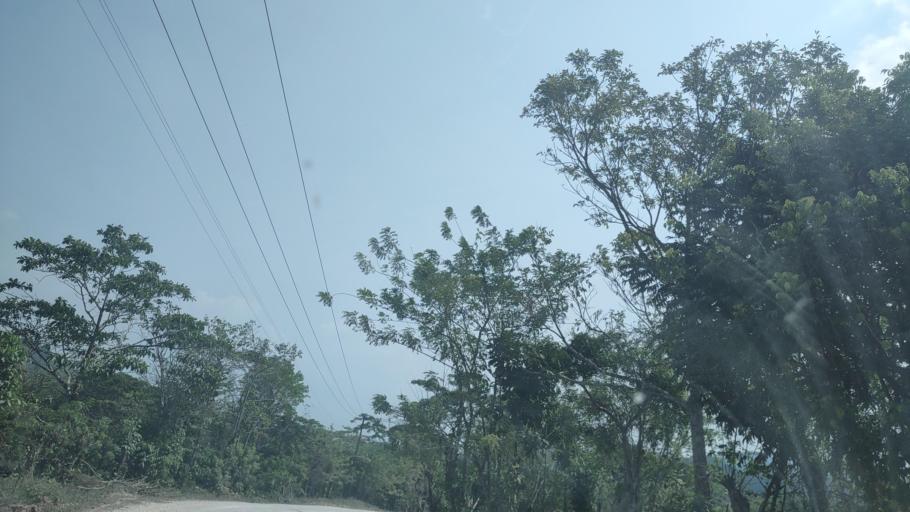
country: MX
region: Tabasco
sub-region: Huimanguillo
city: Francisco Rueda
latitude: 17.5663
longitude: -93.8864
